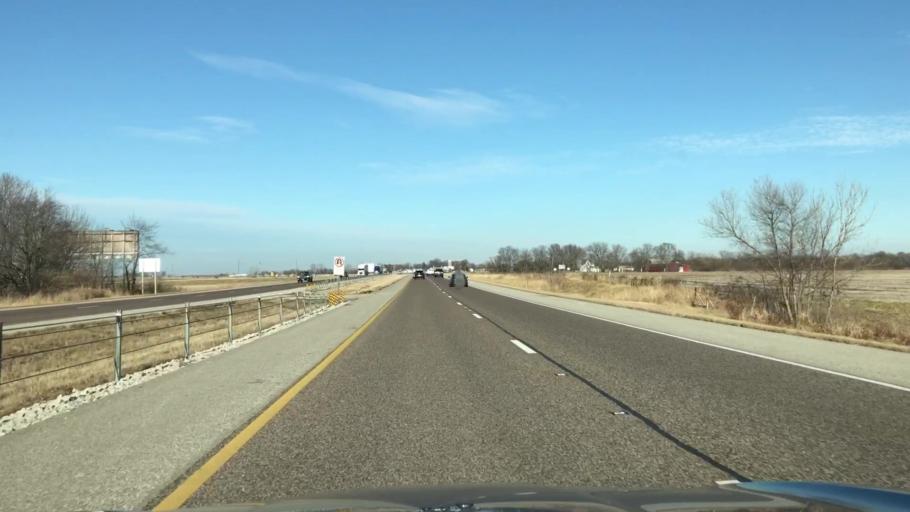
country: US
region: Illinois
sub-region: Madison County
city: Worden
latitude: 38.8989
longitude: -89.8316
